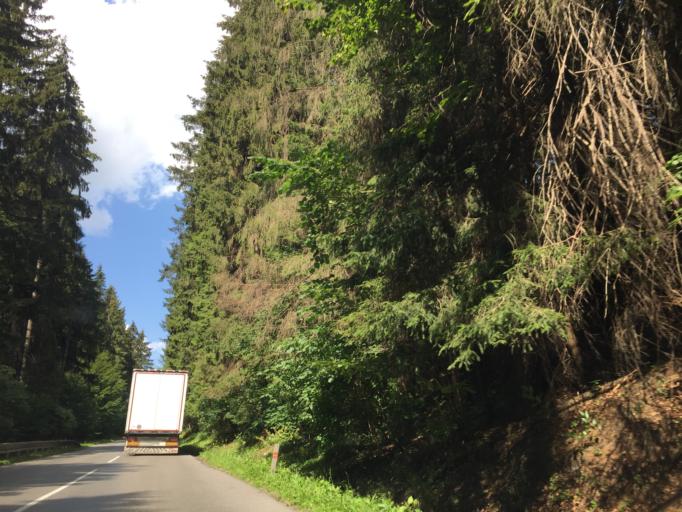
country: SK
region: Zilinsky
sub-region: Okres Dolny Kubin
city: Dolny Kubin
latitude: 49.2886
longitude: 19.3498
